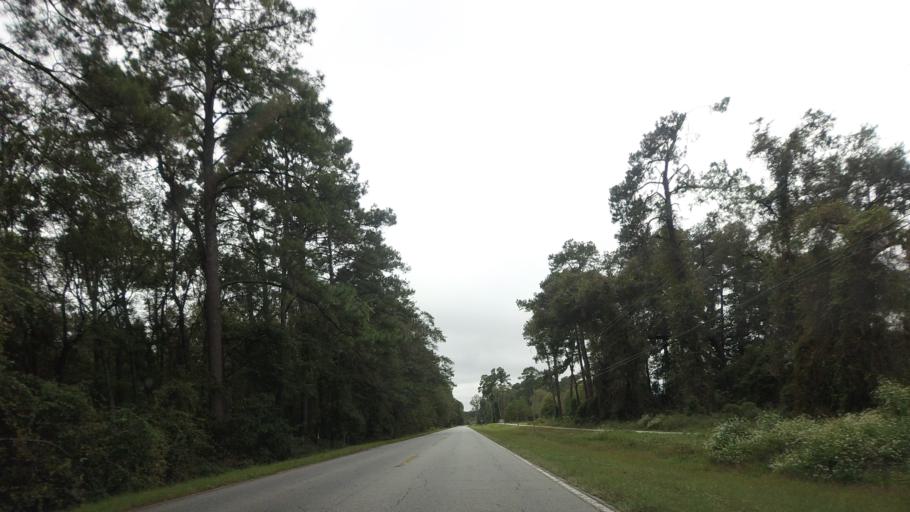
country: US
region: Georgia
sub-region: Lowndes County
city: Valdosta
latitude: 30.8695
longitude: -83.2429
